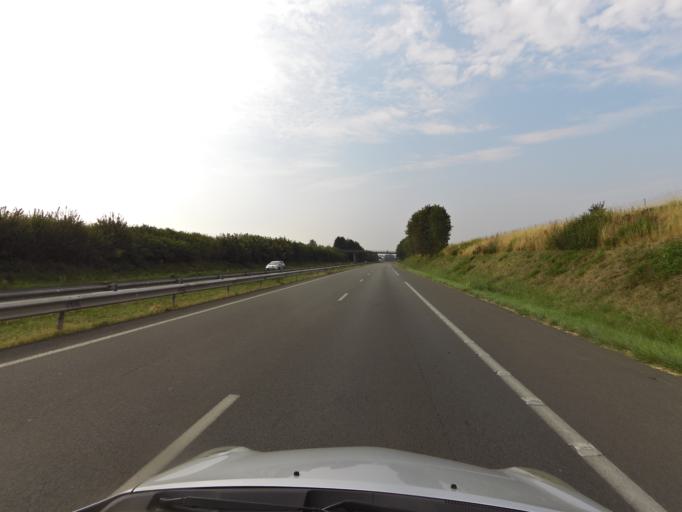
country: FR
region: Nord-Pas-de-Calais
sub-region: Departement du Pas-de-Calais
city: Ecourt-Saint-Quentin
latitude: 50.2316
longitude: 3.0469
